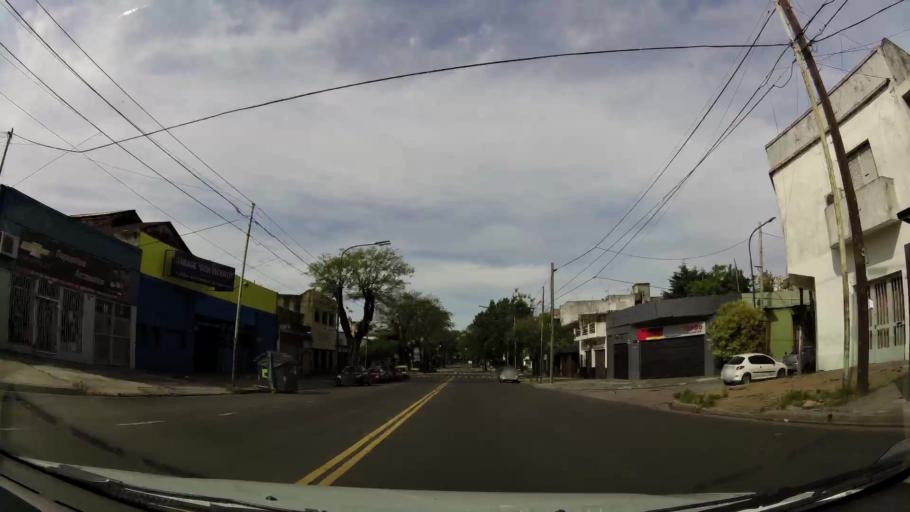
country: AR
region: Buenos Aires F.D.
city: Villa Lugano
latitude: -34.6480
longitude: -58.4878
